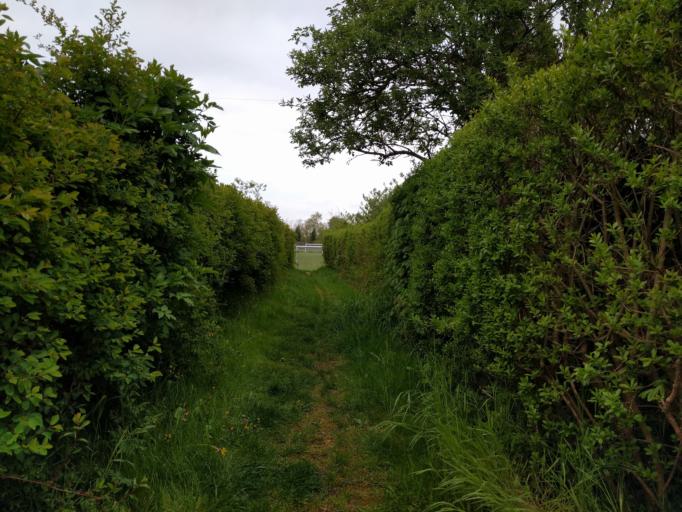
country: DK
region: South Denmark
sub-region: Kerteminde Kommune
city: Langeskov
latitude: 55.3968
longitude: 10.6058
